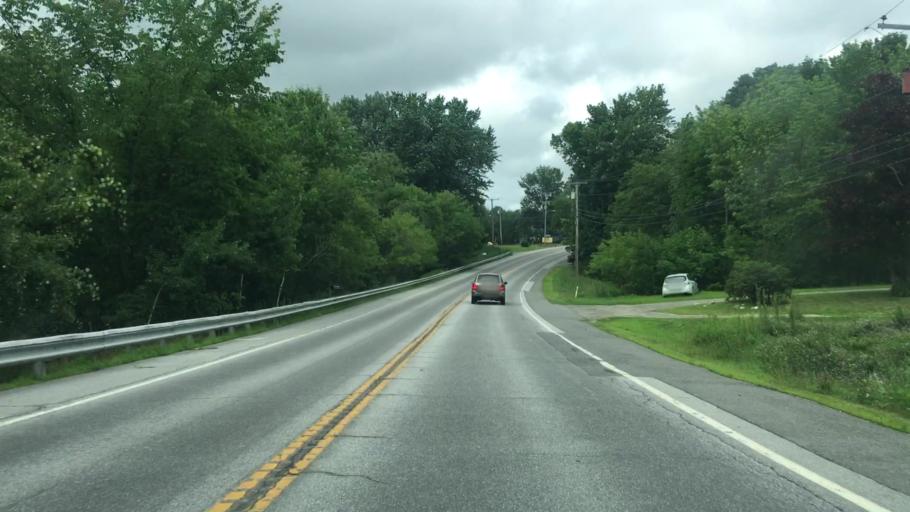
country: US
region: Maine
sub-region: Kennebec County
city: Hallowell
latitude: 44.2809
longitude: -69.7762
